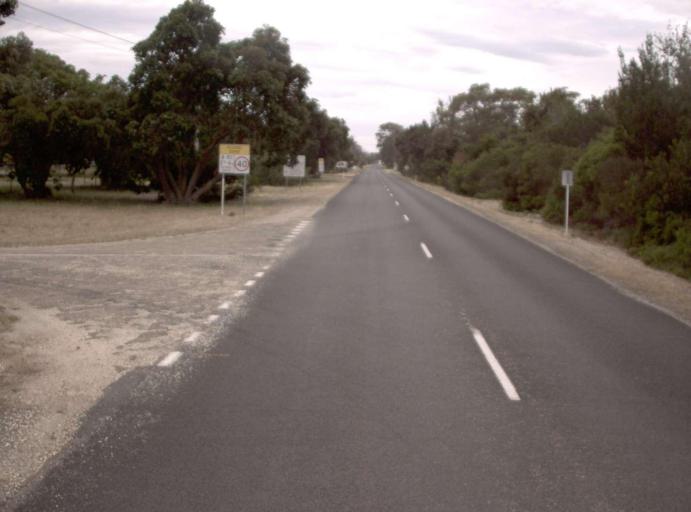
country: AU
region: Victoria
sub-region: East Gippsland
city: Bairnsdale
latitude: -38.0593
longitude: 147.5659
